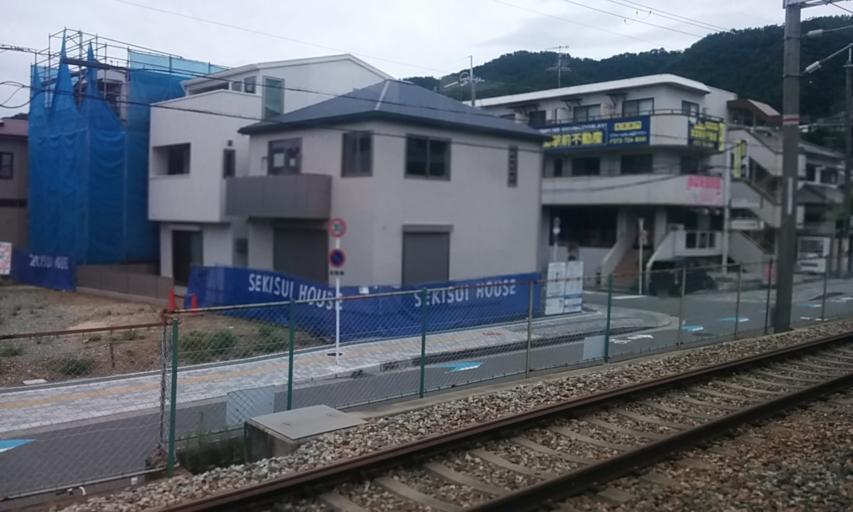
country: JP
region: Osaka
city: Mino
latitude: 34.8333
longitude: 135.4682
